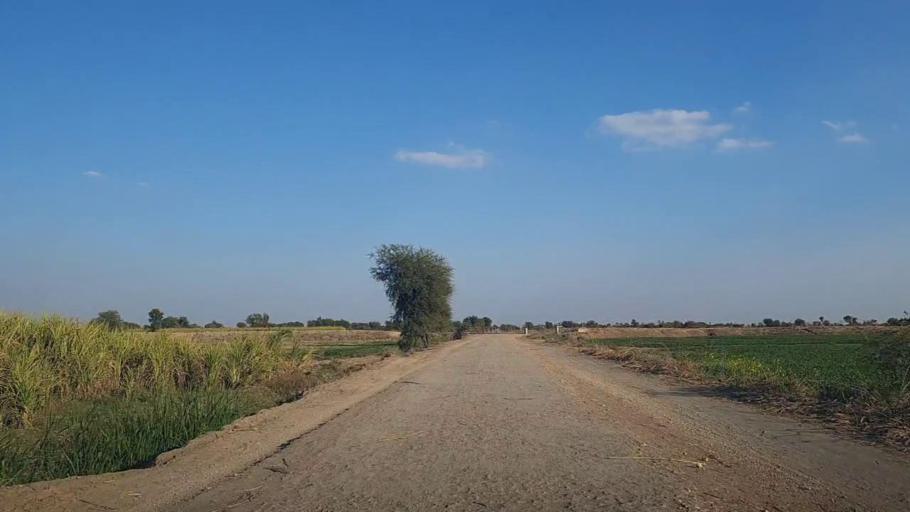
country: PK
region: Sindh
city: Jhol
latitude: 25.9262
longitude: 69.0143
